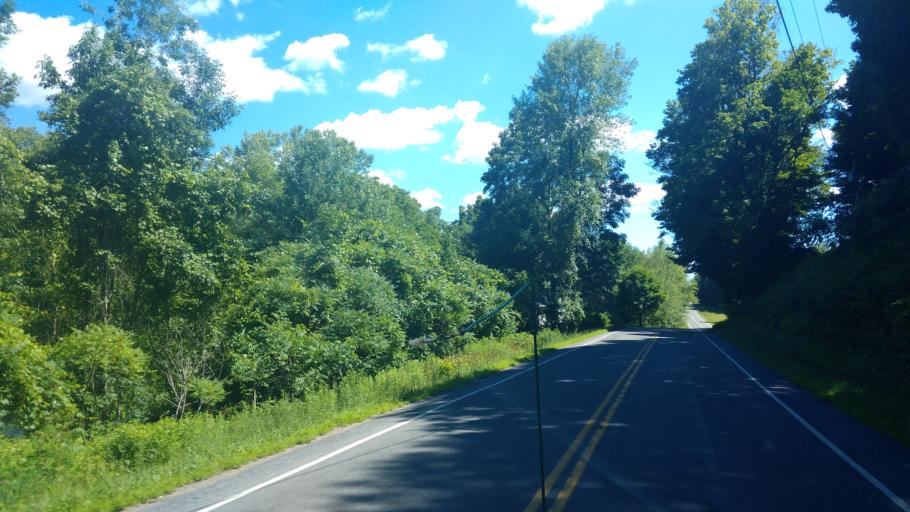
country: US
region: New York
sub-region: Wayne County
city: Sodus
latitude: 43.1686
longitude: -77.0128
